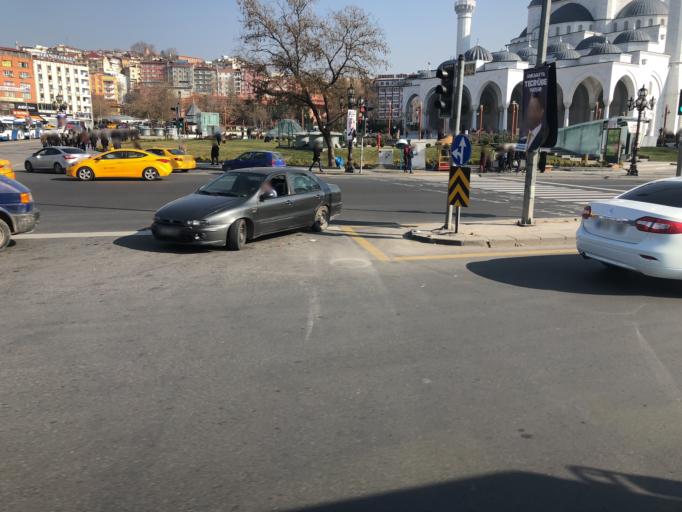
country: TR
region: Ankara
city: Ankara
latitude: 39.9372
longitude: 32.8543
